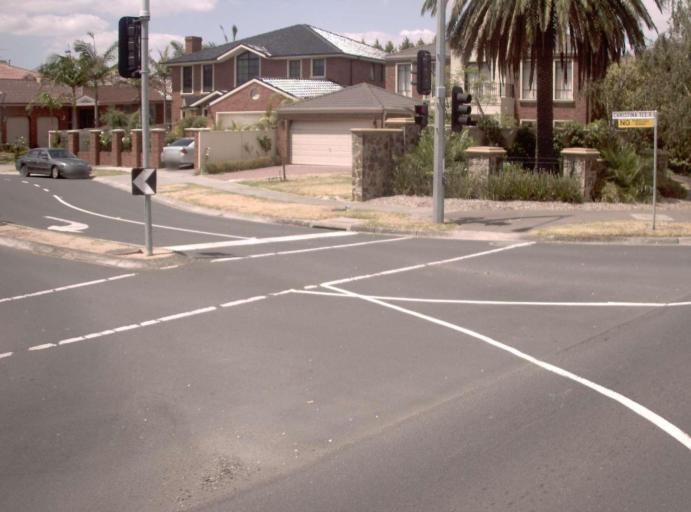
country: AU
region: Victoria
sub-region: Kingston
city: Dingley Village
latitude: -37.9757
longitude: 145.1226
